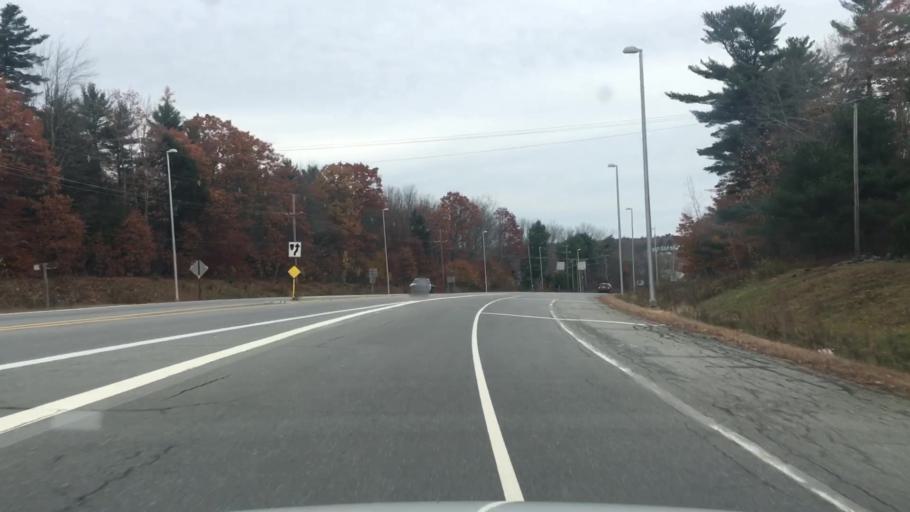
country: US
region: Maine
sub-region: Waldo County
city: Belfast
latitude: 44.4274
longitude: -69.0216
